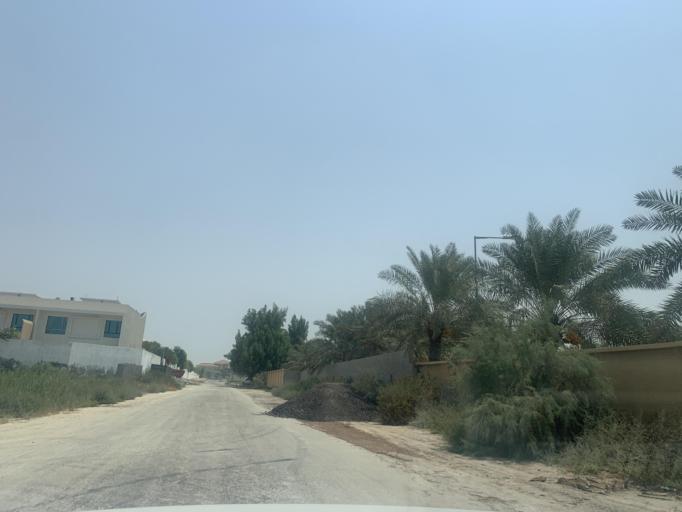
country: BH
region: Central Governorate
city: Madinat Hamad
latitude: 26.1467
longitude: 50.4691
